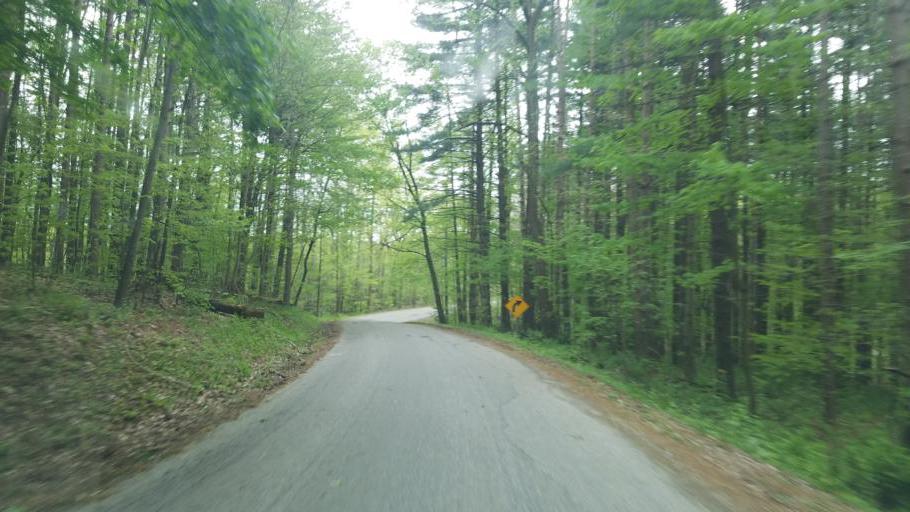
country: US
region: Ohio
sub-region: Ashland County
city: Loudonville
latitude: 40.6078
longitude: -82.2990
